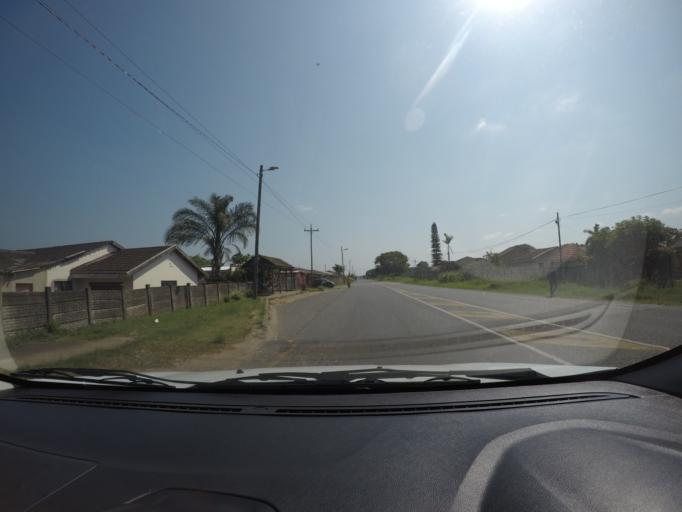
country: ZA
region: KwaZulu-Natal
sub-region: uThungulu District Municipality
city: eSikhawini
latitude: -28.8845
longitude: 31.8863
